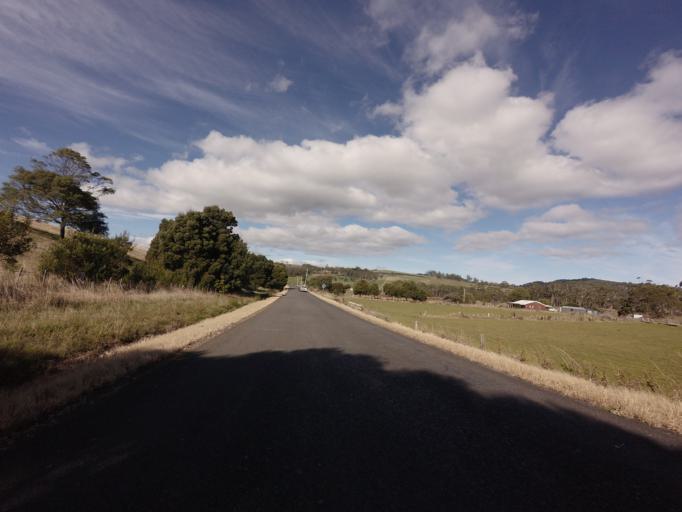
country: AU
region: Tasmania
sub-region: Clarence
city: Sandford
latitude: -43.0246
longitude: 147.7215
